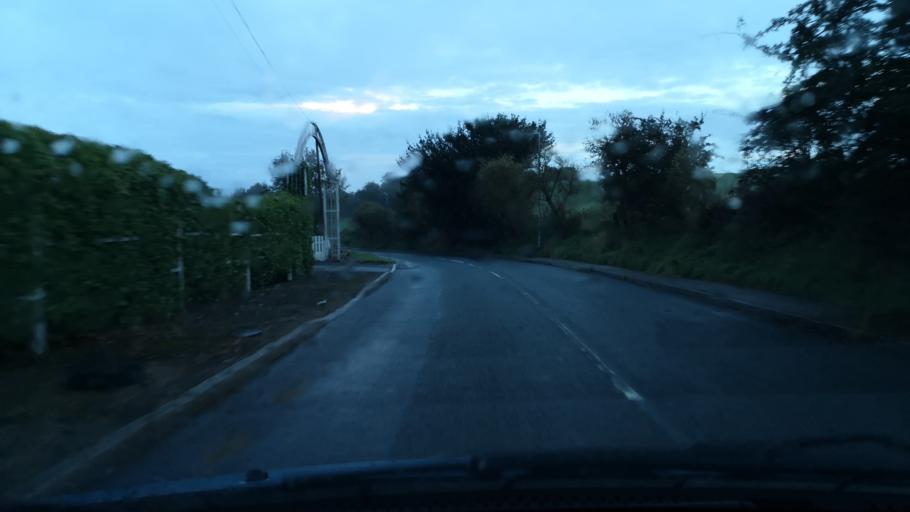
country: GB
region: England
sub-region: Kirklees
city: Batley
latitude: 53.7303
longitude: -1.6394
